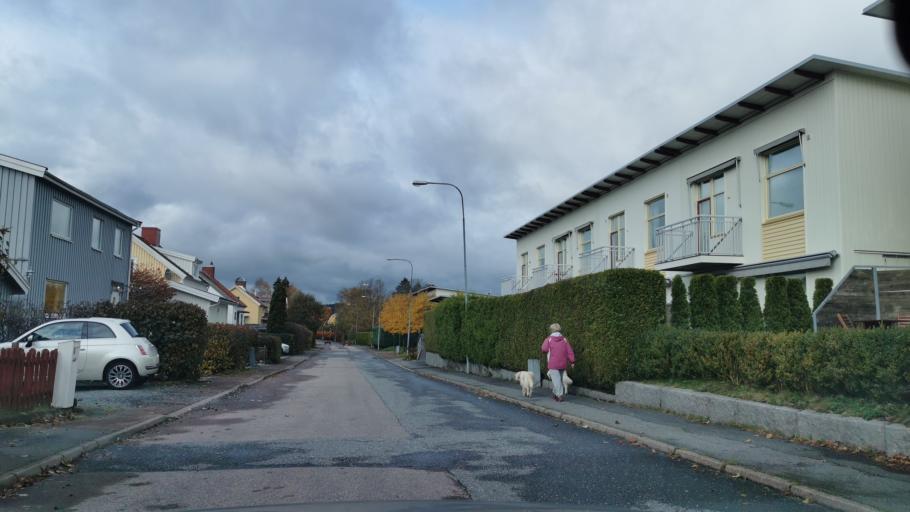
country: SE
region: Vaestra Goetaland
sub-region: Partille Kommun
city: Partille
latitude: 57.7261
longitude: 12.0830
